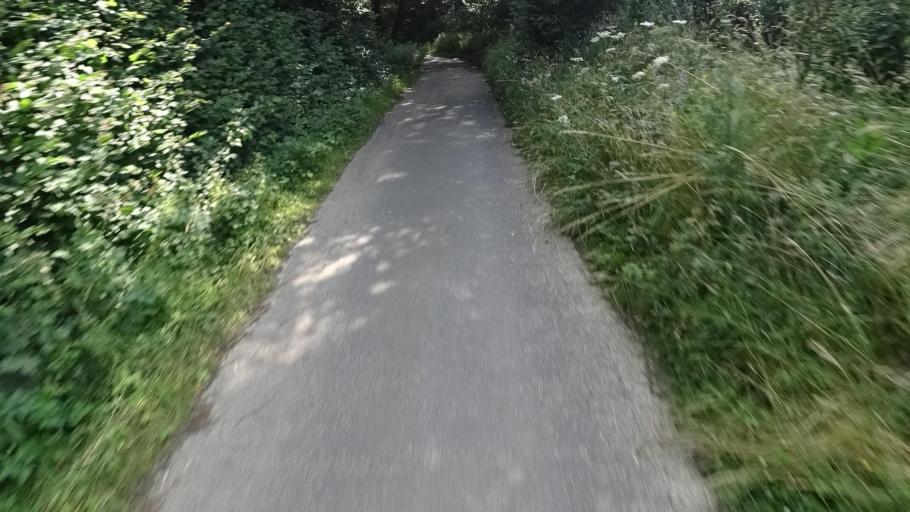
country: DE
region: Rheinland-Pfalz
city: Vettelschoss
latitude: 50.6143
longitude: 7.3470
